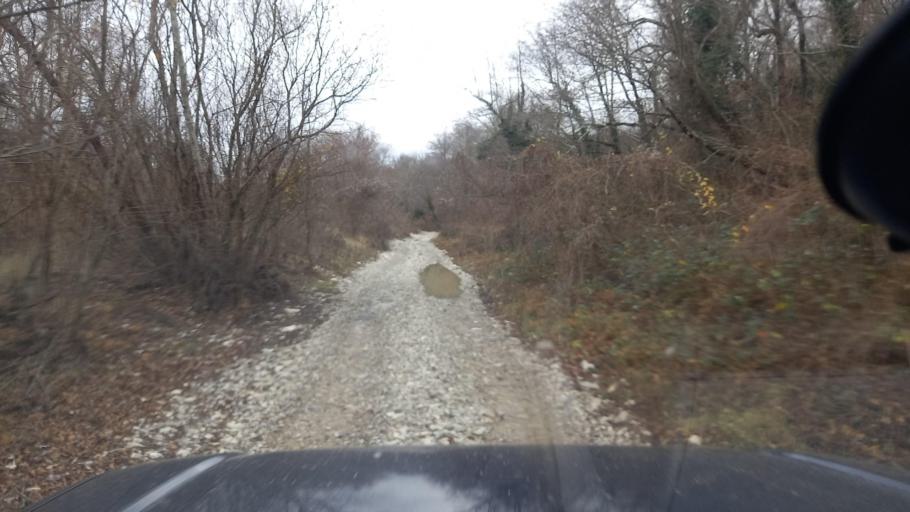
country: RU
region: Krasnodarskiy
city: Pshada
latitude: 44.4943
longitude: 38.4212
